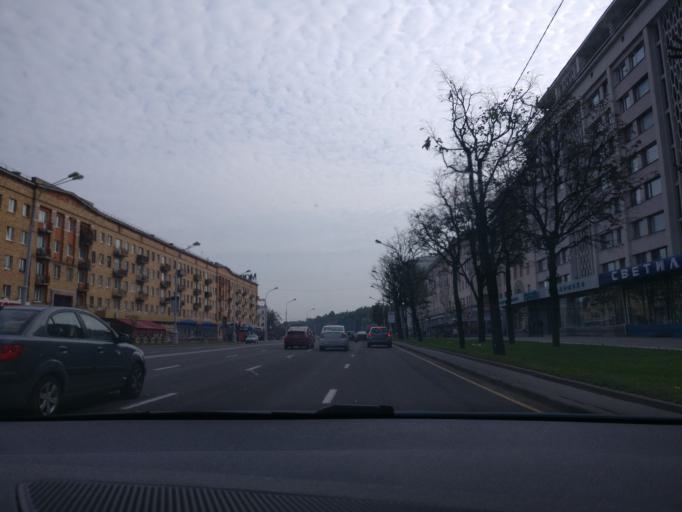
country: BY
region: Minsk
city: Minsk
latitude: 53.9227
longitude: 27.6041
